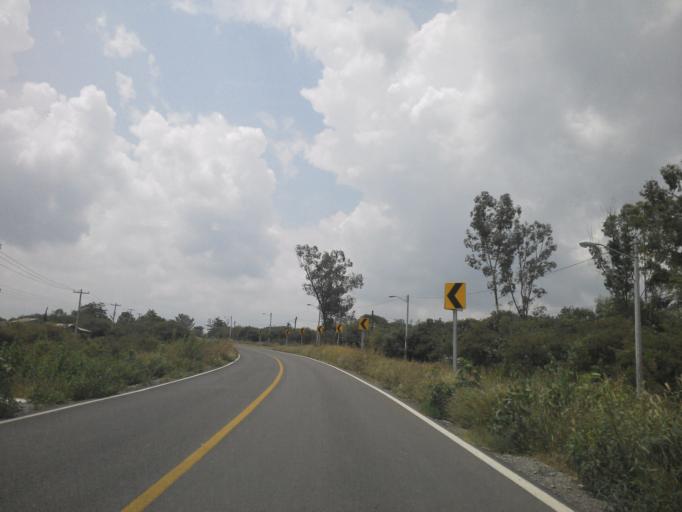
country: MX
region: Guanajuato
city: Ciudad Manuel Doblado
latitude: 20.8298
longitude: -102.0017
